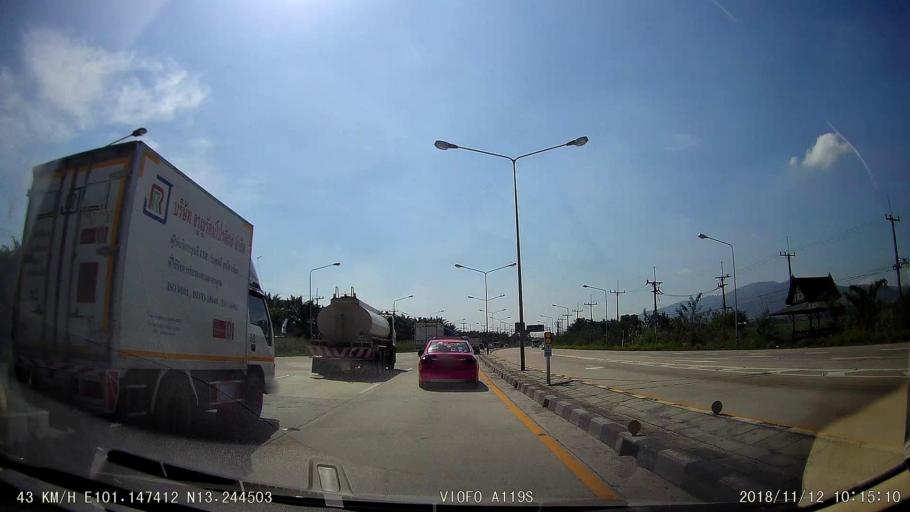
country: TH
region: Chon Buri
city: Ban Bueng
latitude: 13.2444
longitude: 101.1473
